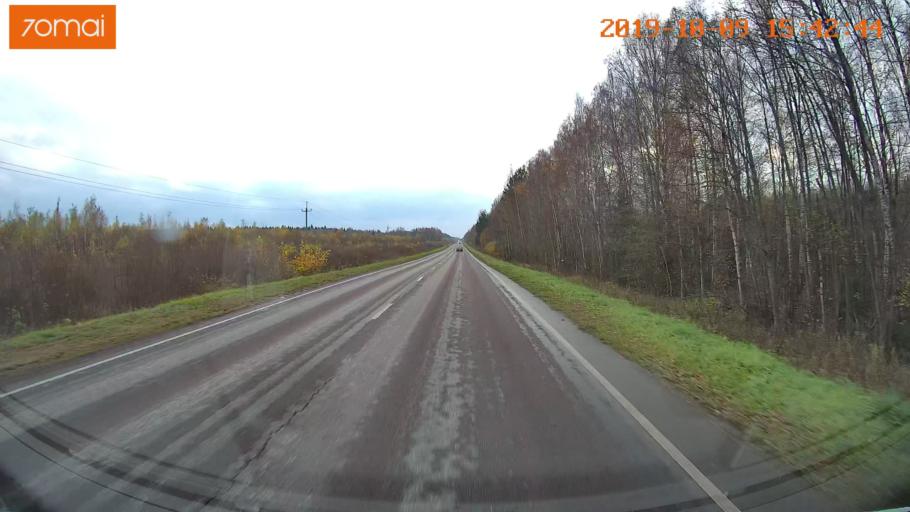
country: RU
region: Kostroma
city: Oktyabr'skiy
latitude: 57.8651
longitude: 41.1013
